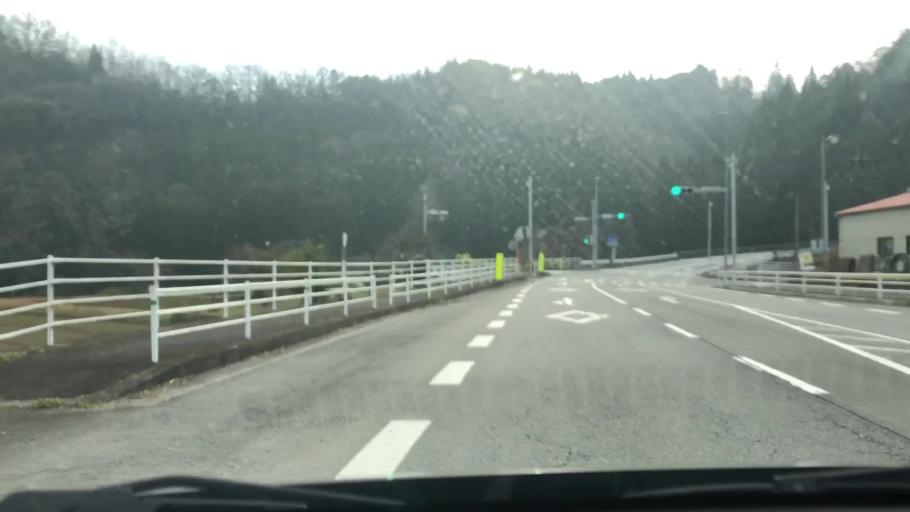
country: JP
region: Oita
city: Takedamachi
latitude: 32.9819
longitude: 131.5480
